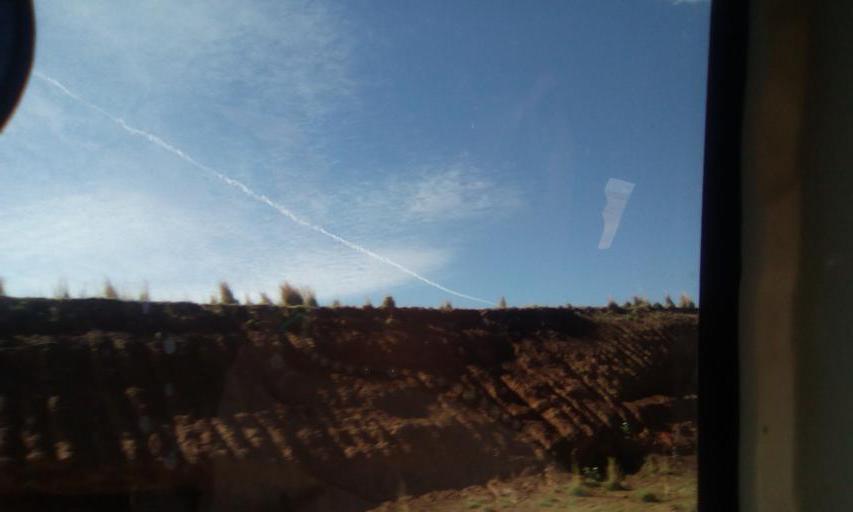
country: LS
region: Qacha's Nek
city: Qacha's Nek
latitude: -30.0419
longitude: 28.2440
